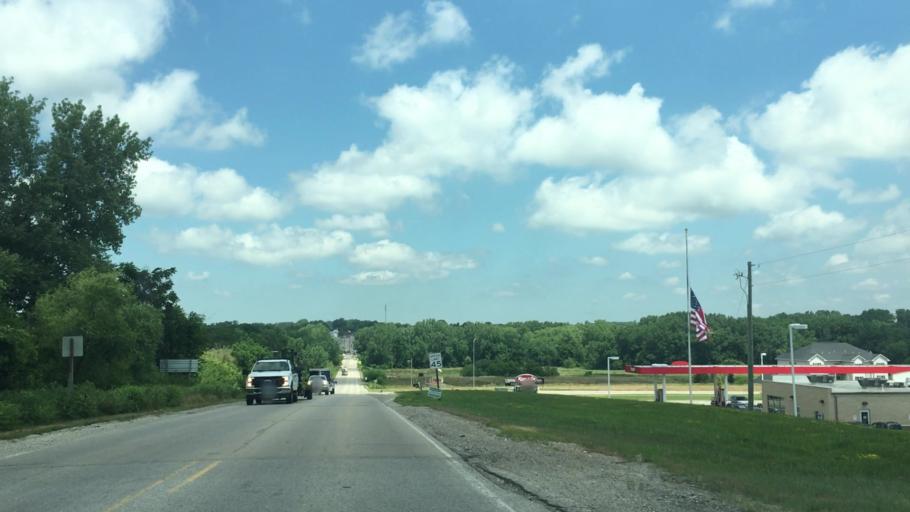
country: US
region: Iowa
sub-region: Johnson County
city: Tiffin
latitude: 41.6958
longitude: -91.6666
